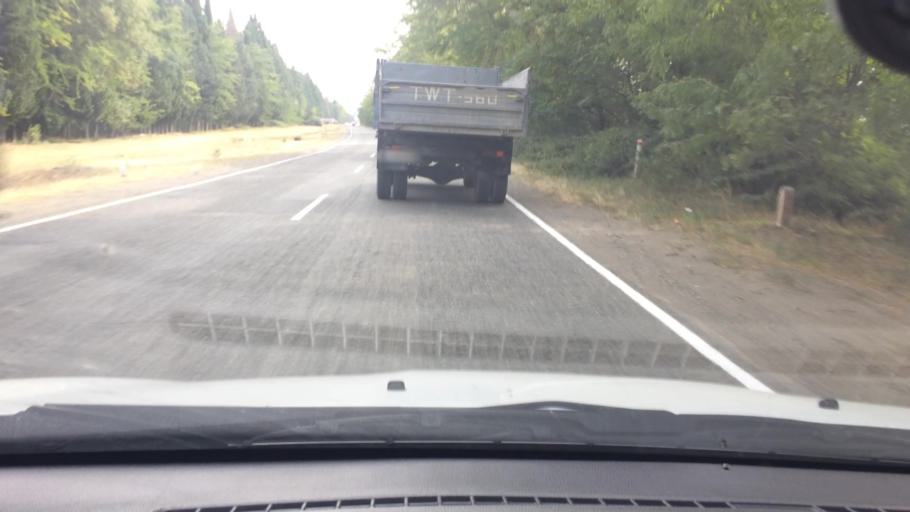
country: GE
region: Kvemo Kartli
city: Rust'avi
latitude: 41.4691
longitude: 44.9803
